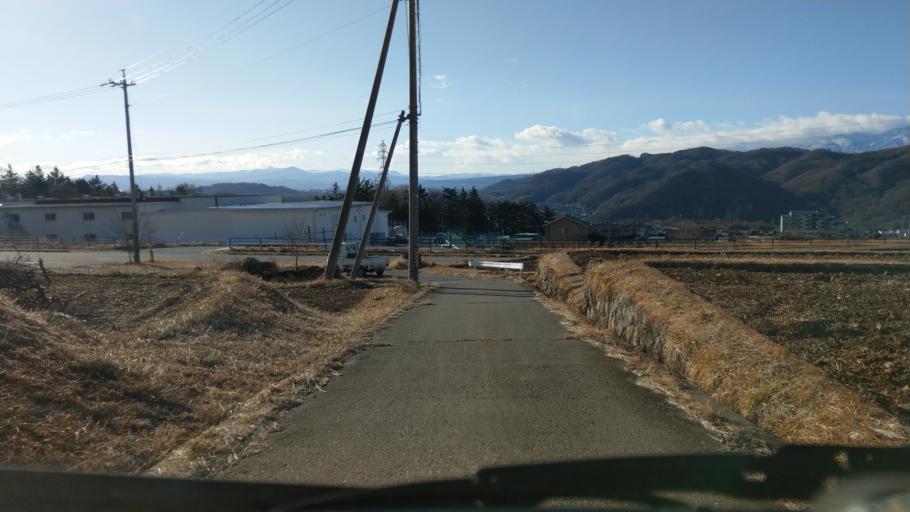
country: JP
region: Nagano
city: Komoro
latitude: 36.3430
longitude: 138.4100
